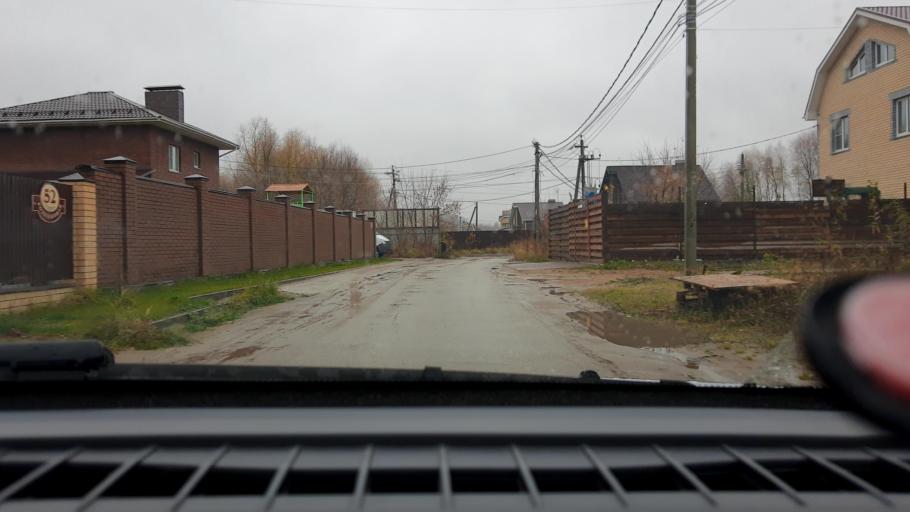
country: RU
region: Nizjnij Novgorod
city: Afonino
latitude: 56.2725
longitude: 44.1001
